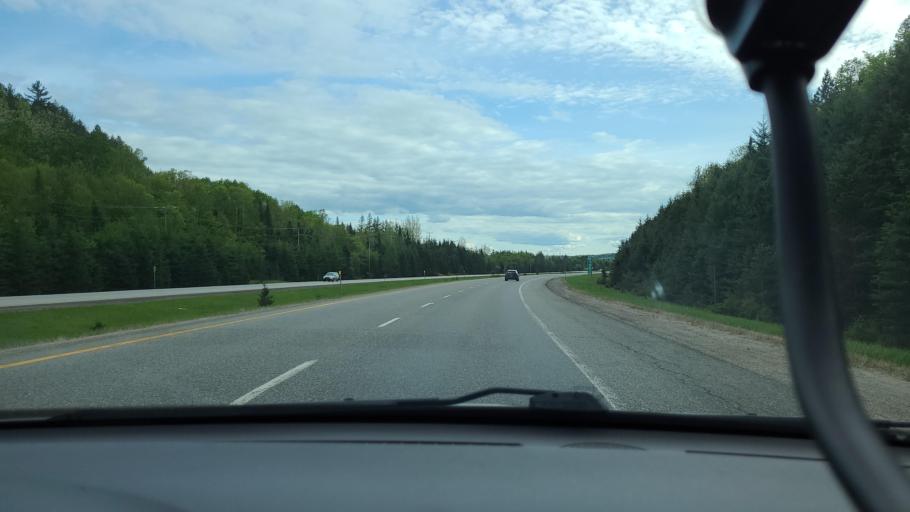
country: CA
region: Quebec
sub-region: Laurentides
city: Labelle
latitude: 46.2180
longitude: -74.7101
